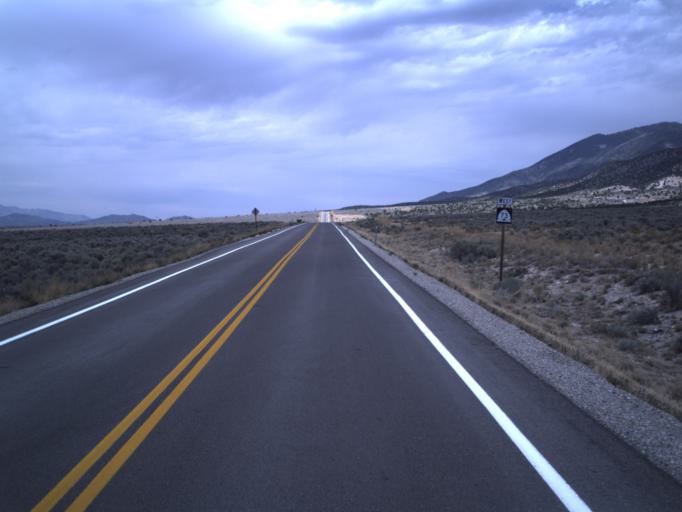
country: US
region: Utah
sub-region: Tooele County
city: Tooele
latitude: 40.2991
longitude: -112.2757
